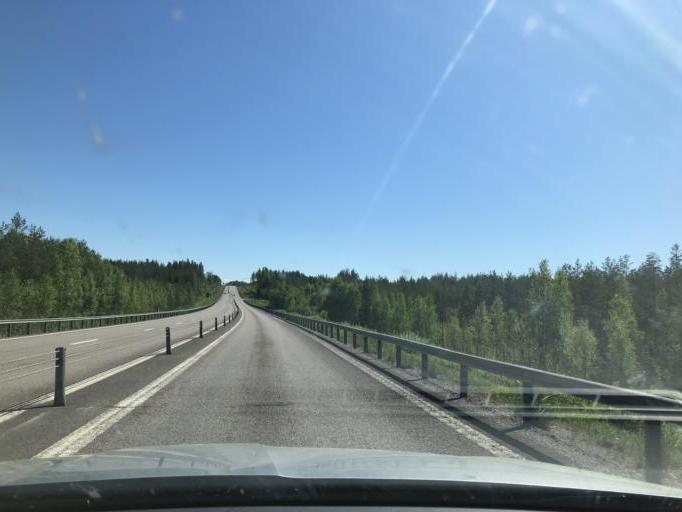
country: SE
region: Norrbotten
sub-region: Kalix Kommun
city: Toere
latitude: 65.9125
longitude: 22.7992
